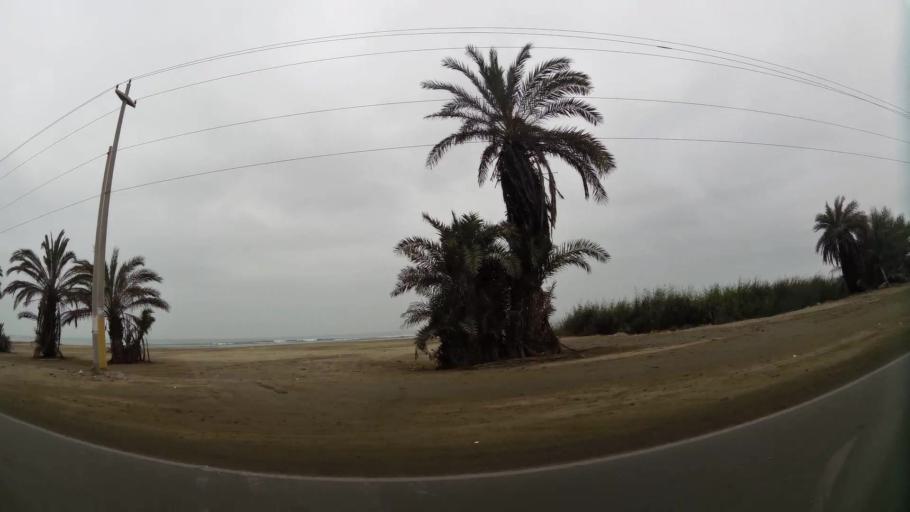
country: PE
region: Ica
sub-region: Provincia de Pisco
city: Pisco
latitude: -13.7227
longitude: -76.2217
